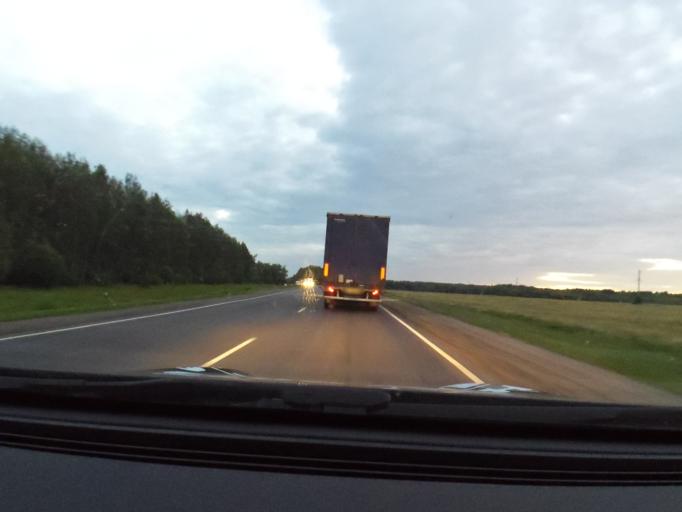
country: RU
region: Chuvashia
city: Yadrin
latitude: 56.0023
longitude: 46.0583
